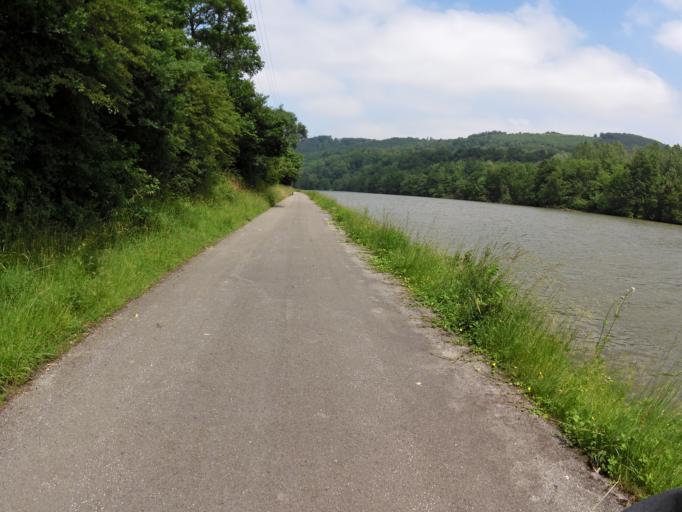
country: BE
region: Wallonia
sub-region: Province de Namur
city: Hastiere-Lavaux
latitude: 50.1835
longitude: 4.8236
